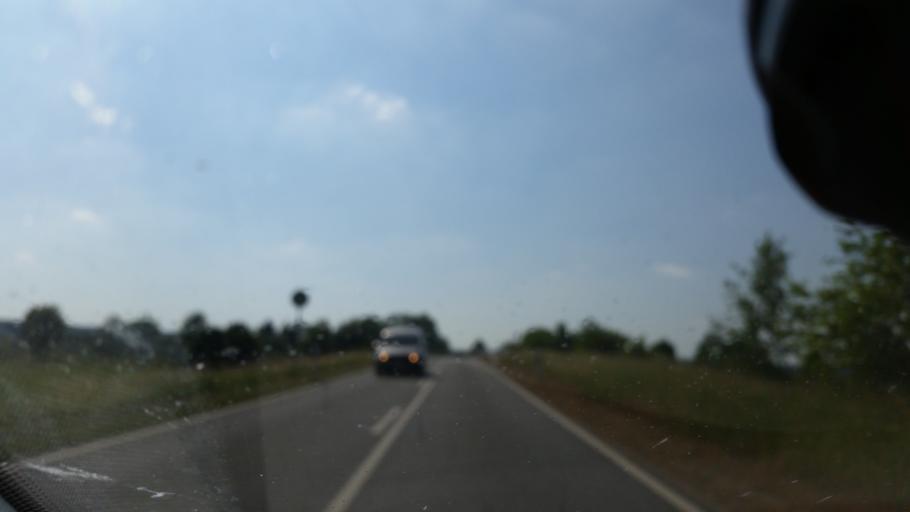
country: DE
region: Lower Saxony
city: Lehre
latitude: 52.3207
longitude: 10.6910
